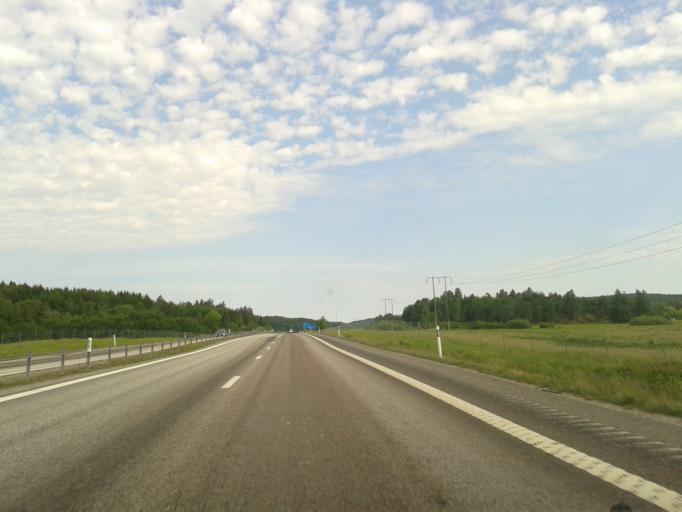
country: SE
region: Vaestra Goetaland
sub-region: Munkedals Kommun
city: Munkedal
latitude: 58.5072
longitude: 11.5605
